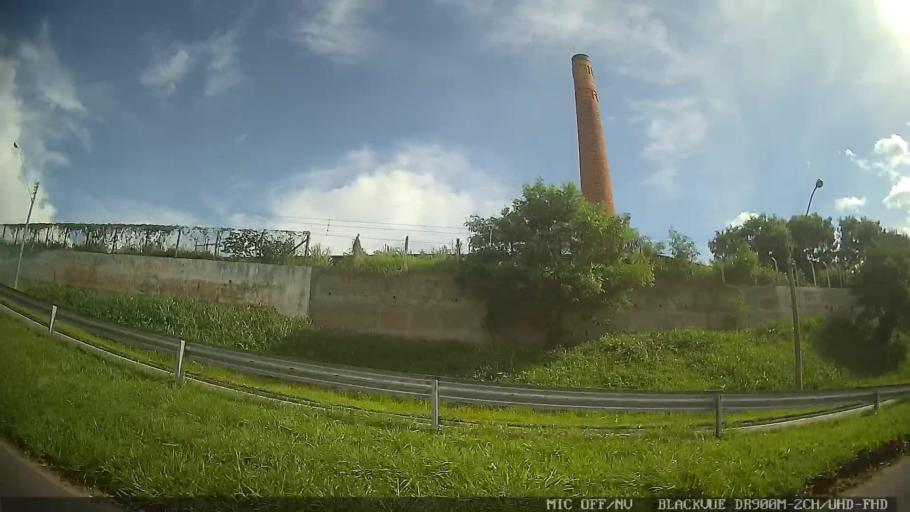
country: BR
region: Sao Paulo
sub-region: Laranjal Paulista
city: Laranjal Paulista
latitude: -23.0400
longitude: -47.8343
